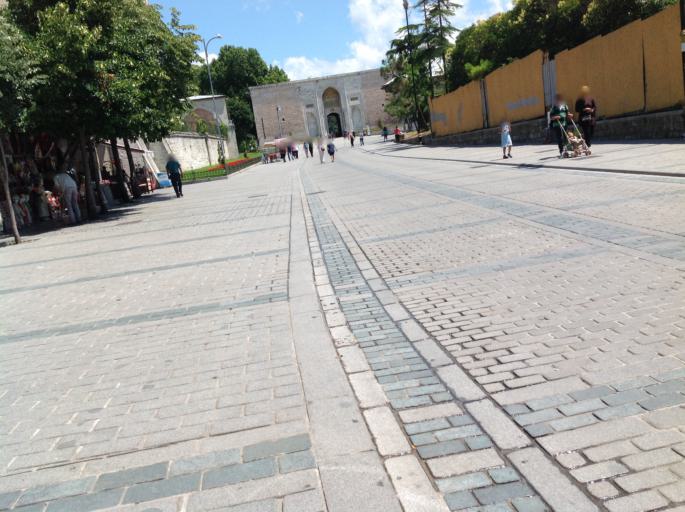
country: TR
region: Istanbul
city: Eminoenue
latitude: 41.0076
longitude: 28.9800
